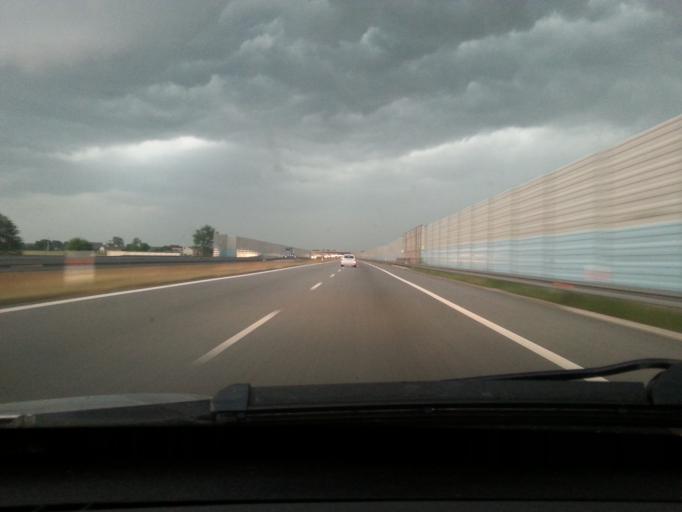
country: PL
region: Lodz Voivodeship
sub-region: powiat Lowicki
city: Lyszkowice
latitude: 51.9829
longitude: 19.8867
